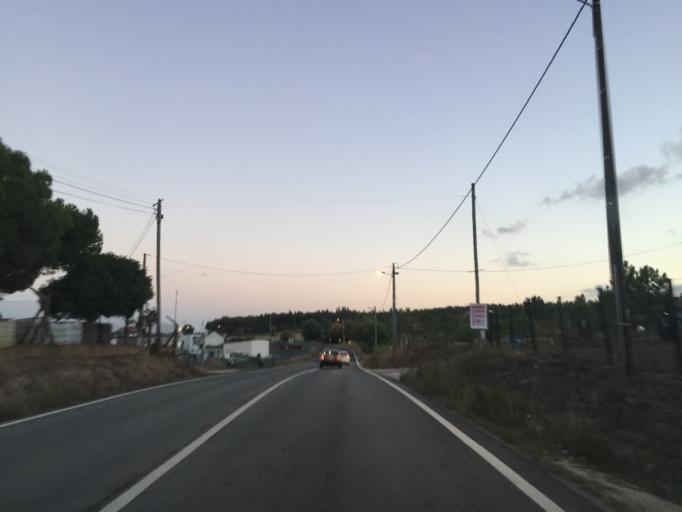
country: PT
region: Lisbon
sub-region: Alenquer
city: Alenquer
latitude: 39.1316
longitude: -8.9958
